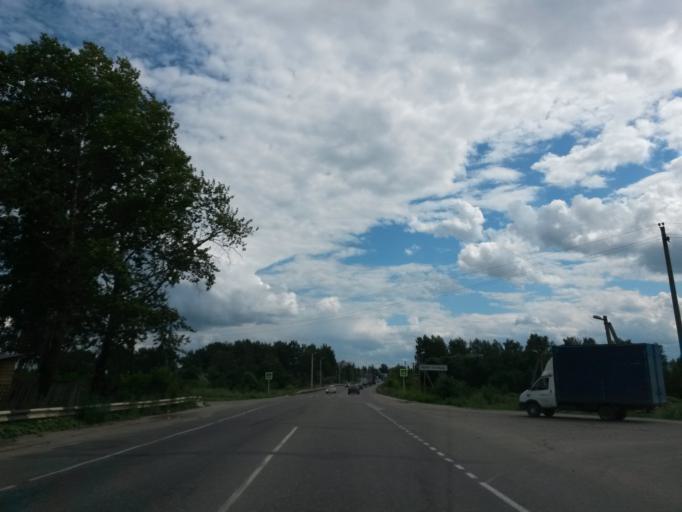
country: RU
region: Ivanovo
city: Novo-Talitsy
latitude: 57.0096
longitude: 40.8386
